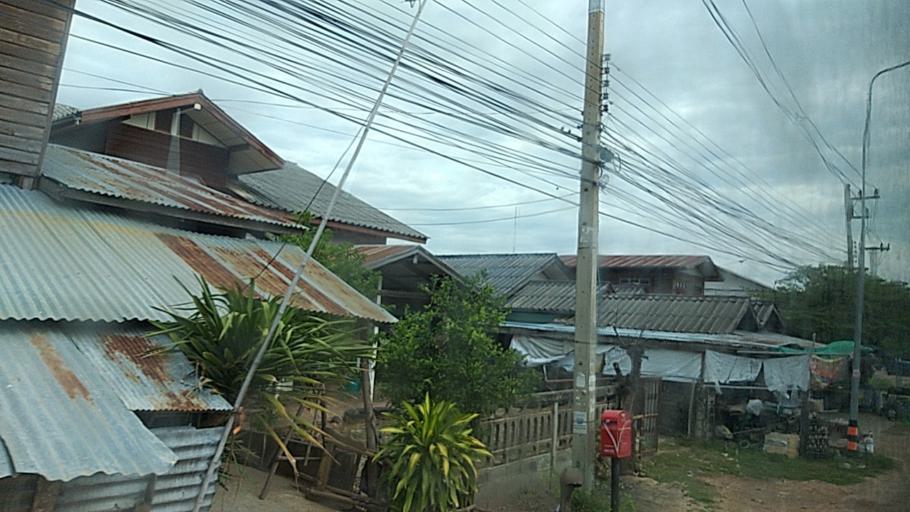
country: TH
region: Maha Sarakham
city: Kantharawichai
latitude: 16.3373
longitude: 103.1914
